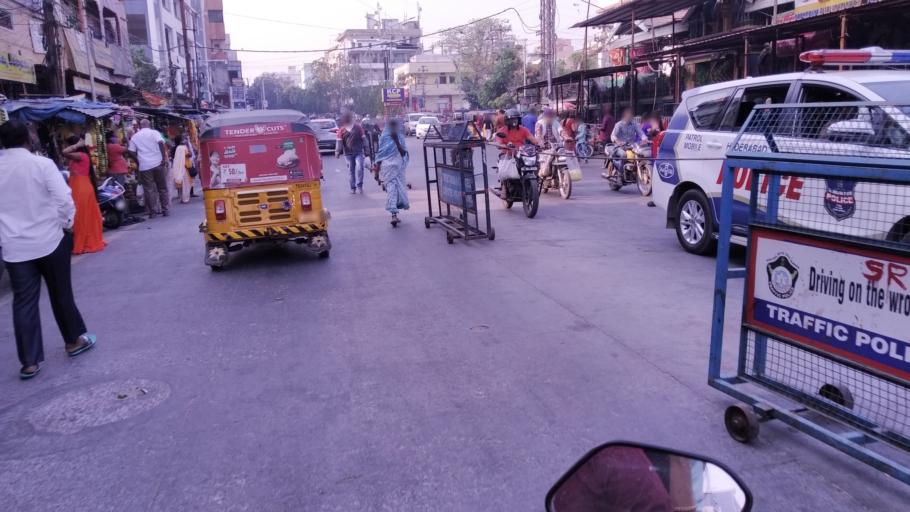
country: IN
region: Telangana
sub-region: Rangareddi
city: Kukatpalli
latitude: 17.4475
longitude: 78.4494
